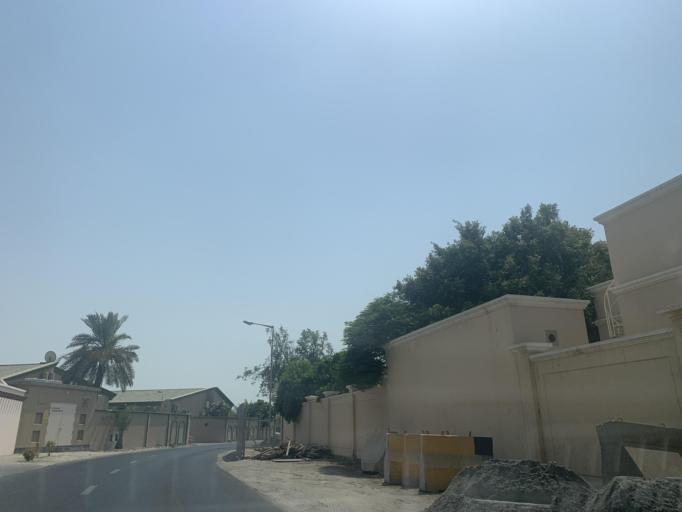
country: BH
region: Manama
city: Jidd Hafs
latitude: 26.1994
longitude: 50.4964
